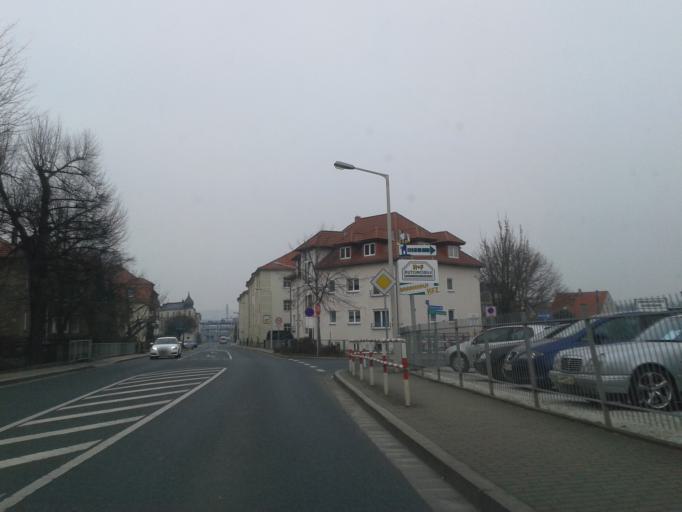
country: DE
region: Saxony
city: Freital
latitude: 50.9977
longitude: 13.6459
